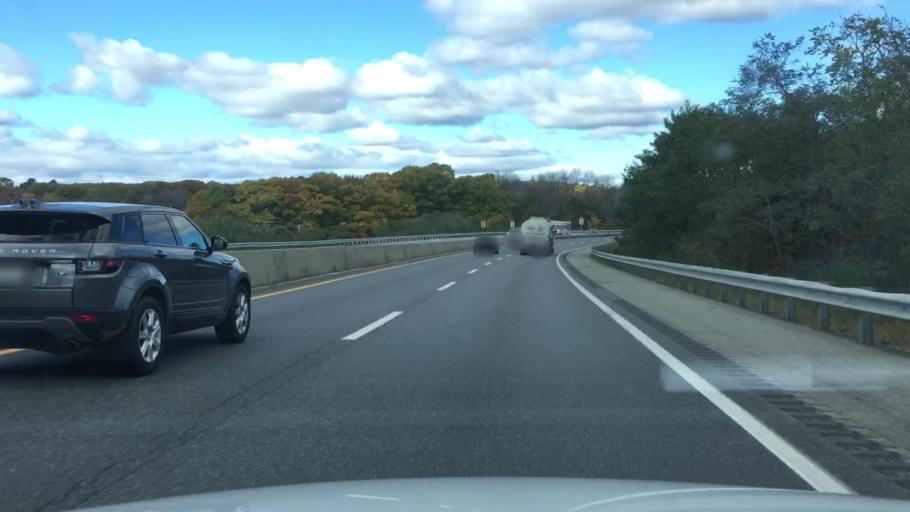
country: US
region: Maine
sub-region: Cumberland County
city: Portland
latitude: 43.6879
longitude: -70.2540
